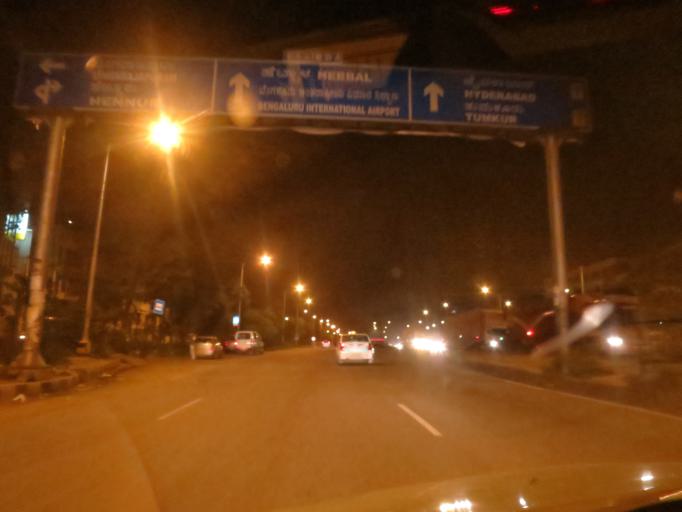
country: IN
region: Karnataka
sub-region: Bangalore Urban
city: Bangalore
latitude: 13.0264
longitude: 77.6366
